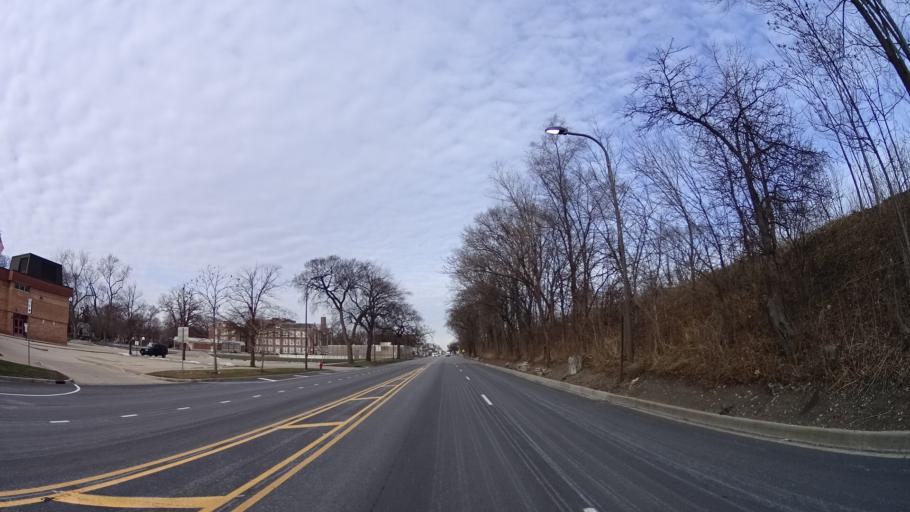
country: US
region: Illinois
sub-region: Cook County
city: Evanston
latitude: 42.0604
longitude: -87.6954
